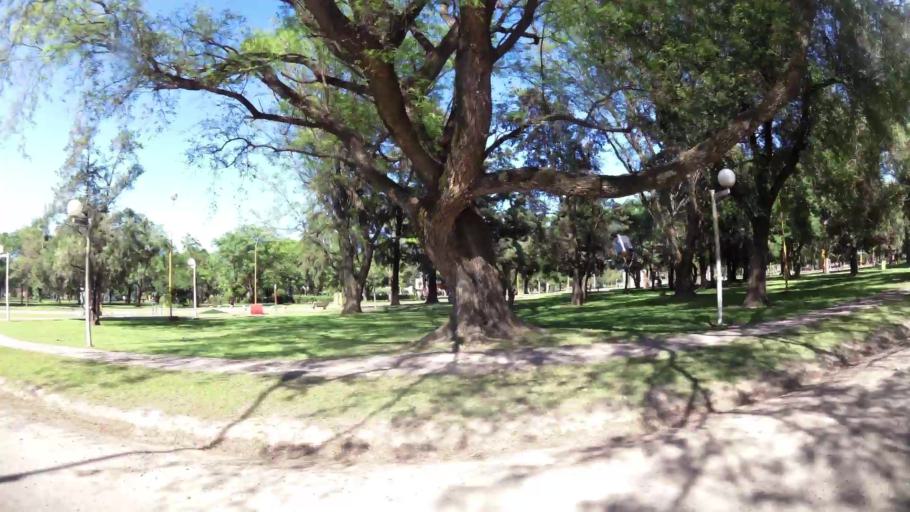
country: AR
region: Santa Fe
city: Esperanza
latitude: -31.4484
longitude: -60.9173
